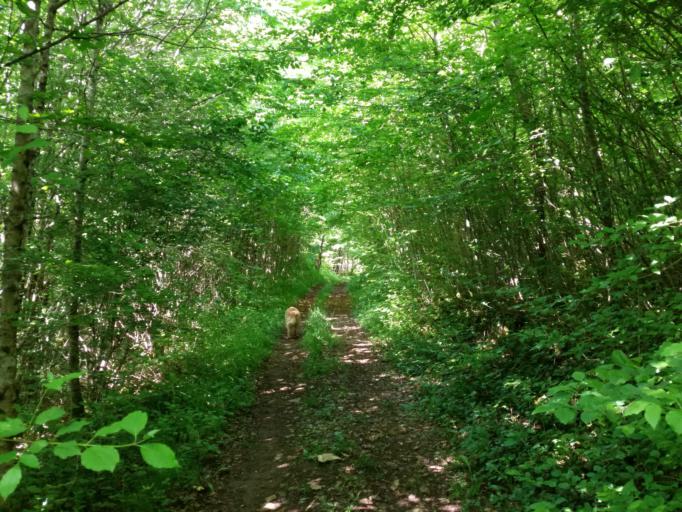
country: FR
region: Franche-Comte
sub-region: Departement du Doubs
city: Quingey
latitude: 47.0374
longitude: 5.9695
